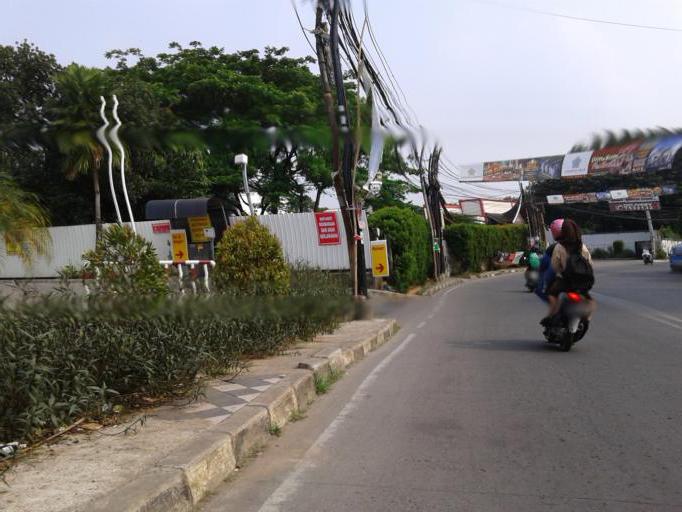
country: ID
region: West Java
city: Pamulang
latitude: -6.3276
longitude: 106.7852
